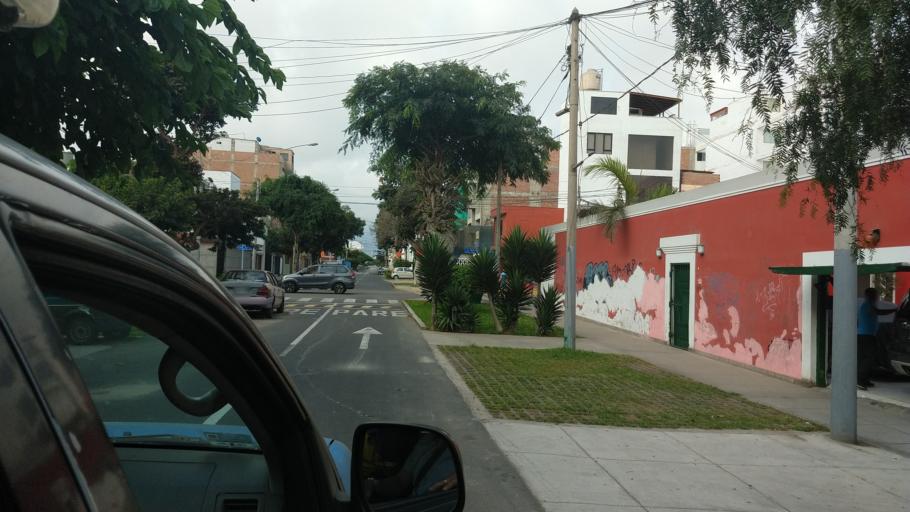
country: PE
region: Lima
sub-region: Lima
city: San Isidro
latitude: -12.0909
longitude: -77.0789
